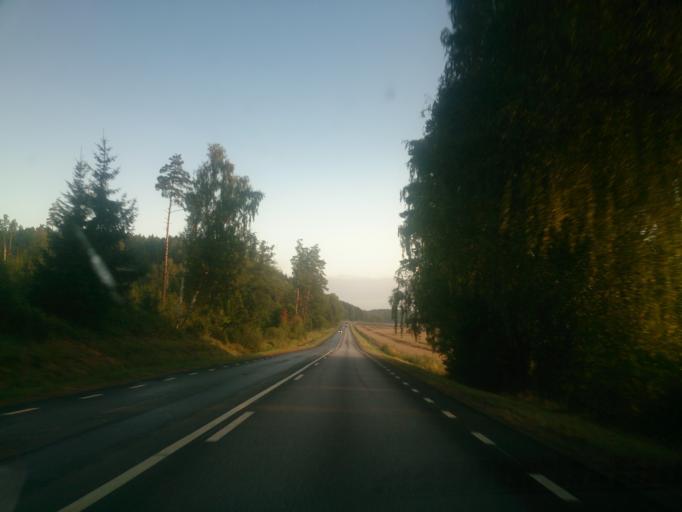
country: SE
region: Soedermanland
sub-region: Nykopings Kommun
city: Nykoping
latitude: 58.8031
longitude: 17.0824
